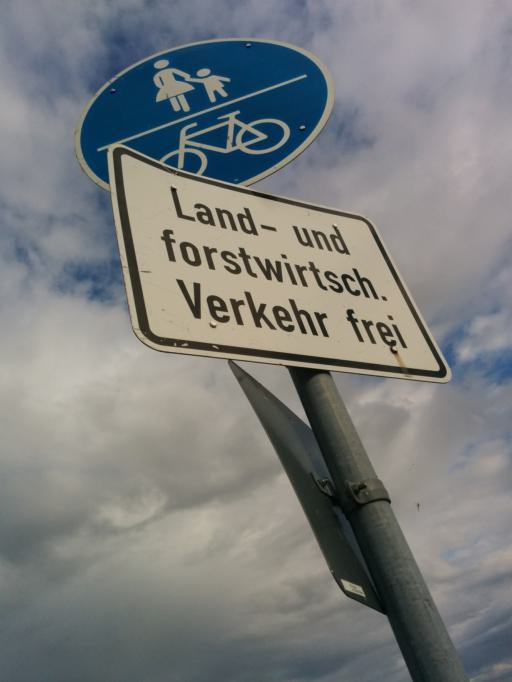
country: DE
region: Saxony
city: Guttau
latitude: 51.2564
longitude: 14.5337
